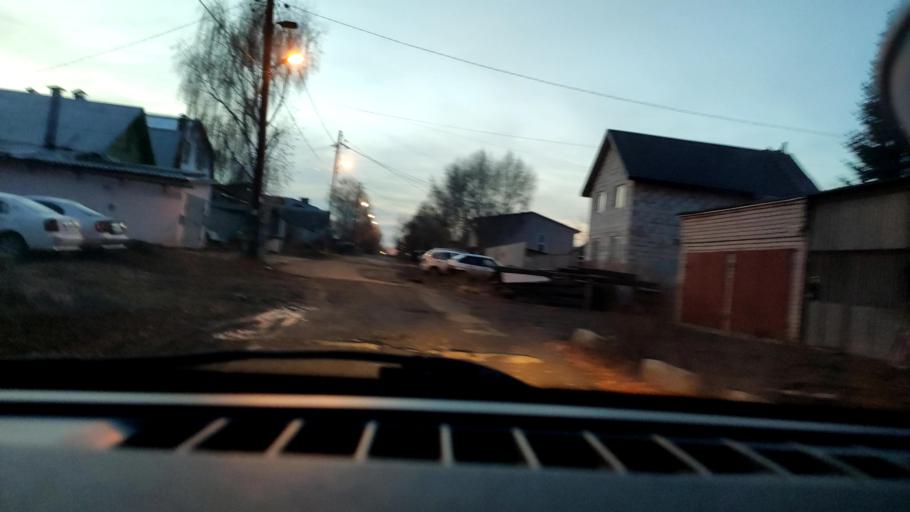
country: RU
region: Samara
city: Petra-Dubrava
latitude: 53.2629
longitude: 50.3330
